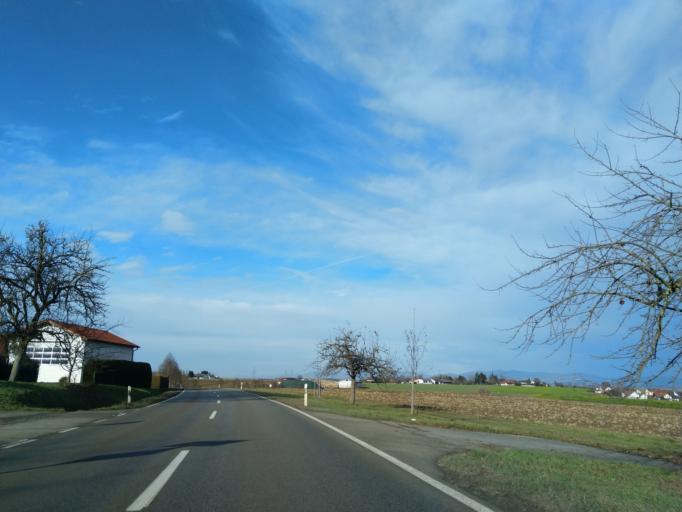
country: DE
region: Bavaria
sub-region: Lower Bavaria
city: Kunzing
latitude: 48.6407
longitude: 13.0496
